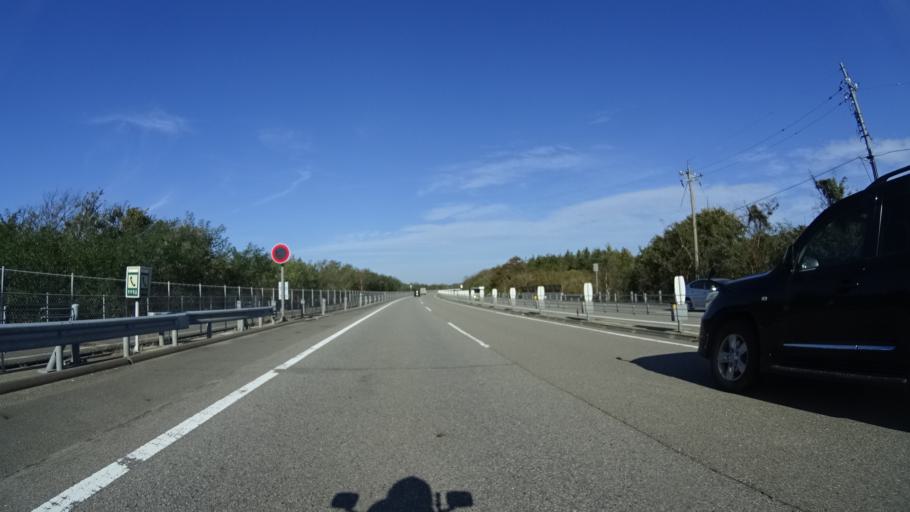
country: JP
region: Ishikawa
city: Tsubata
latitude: 36.6876
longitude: 136.6627
